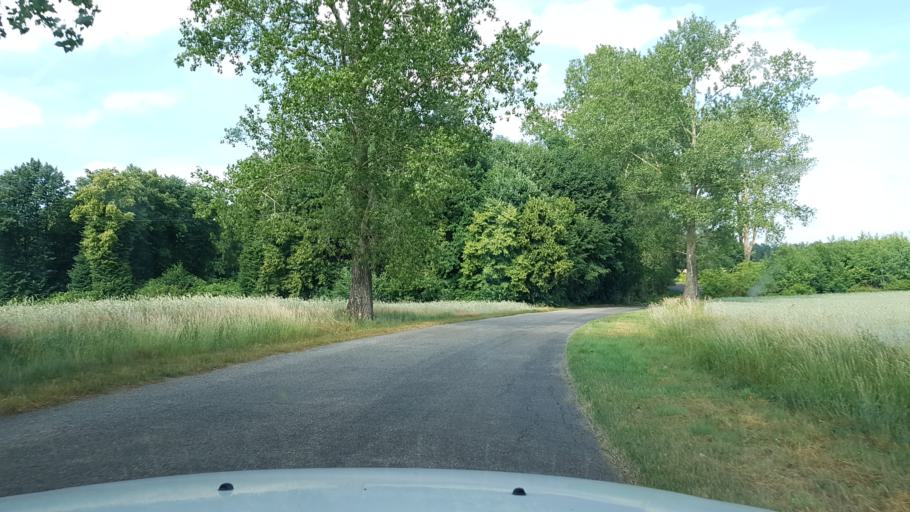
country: PL
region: West Pomeranian Voivodeship
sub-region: Powiat goleniowski
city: Osina
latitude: 53.5811
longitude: 14.9826
